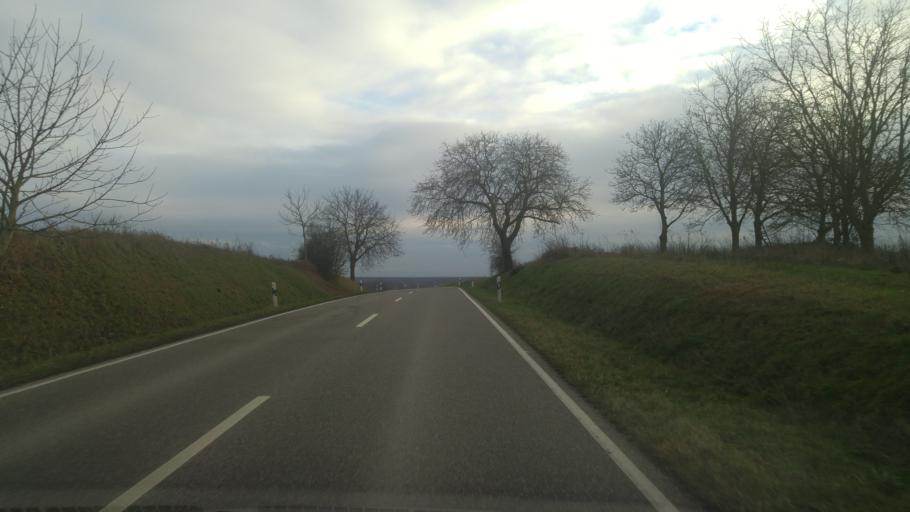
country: DE
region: Rheinland-Pfalz
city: Minfeld
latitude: 49.0799
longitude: 8.1288
